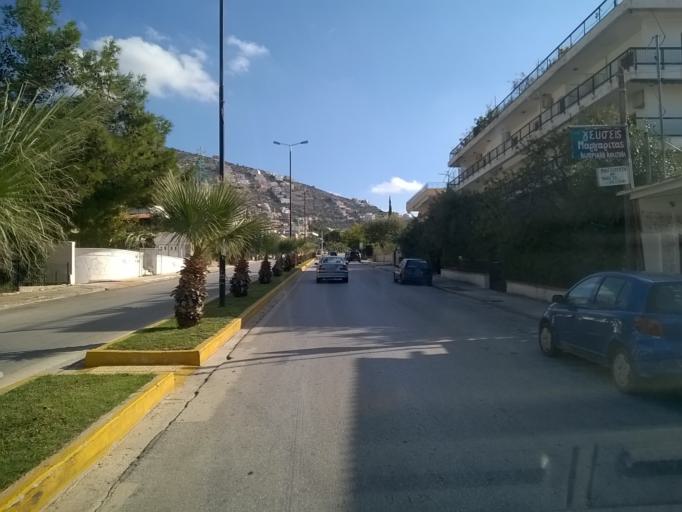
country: GR
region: Attica
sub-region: Nomarchia Anatolikis Attikis
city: Saronida
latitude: 37.7477
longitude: 23.9126
